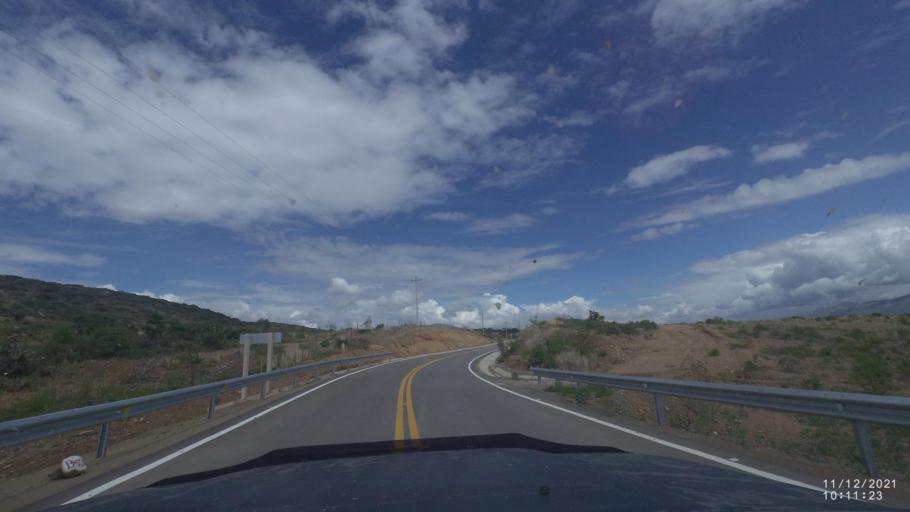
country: BO
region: Cochabamba
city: Tarata
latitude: -17.6371
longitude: -65.9864
